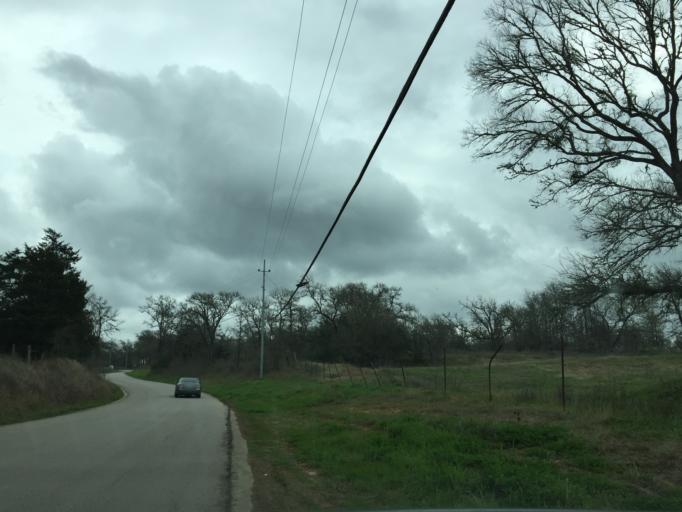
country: US
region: Texas
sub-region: Bastrop County
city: Bastrop
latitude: 30.1212
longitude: -97.3089
